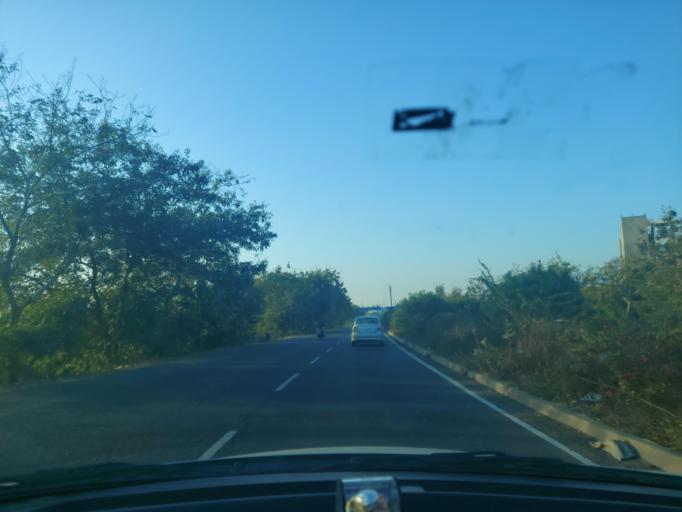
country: IN
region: Madhya Pradesh
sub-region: Ujjain
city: Ujjain
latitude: 23.0991
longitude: 75.8108
